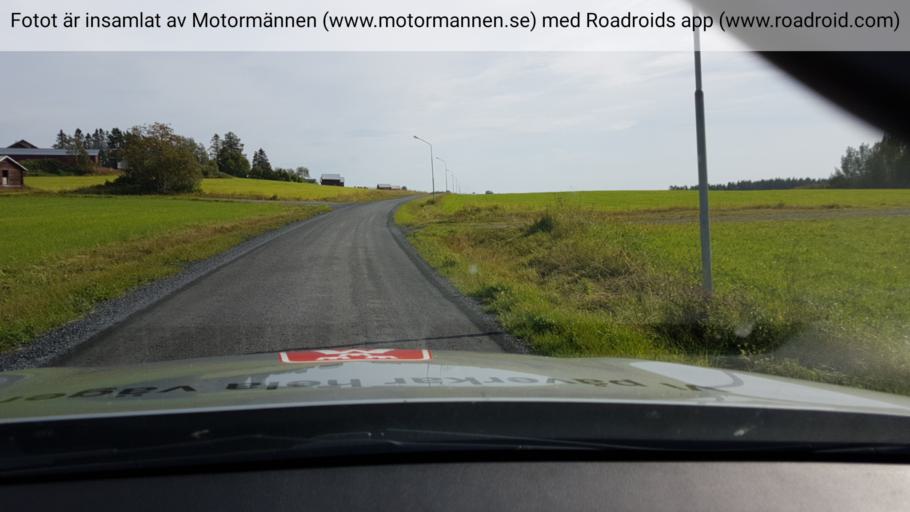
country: SE
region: Jaemtland
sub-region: Krokoms Kommun
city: Valla
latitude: 63.3640
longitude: 13.9601
